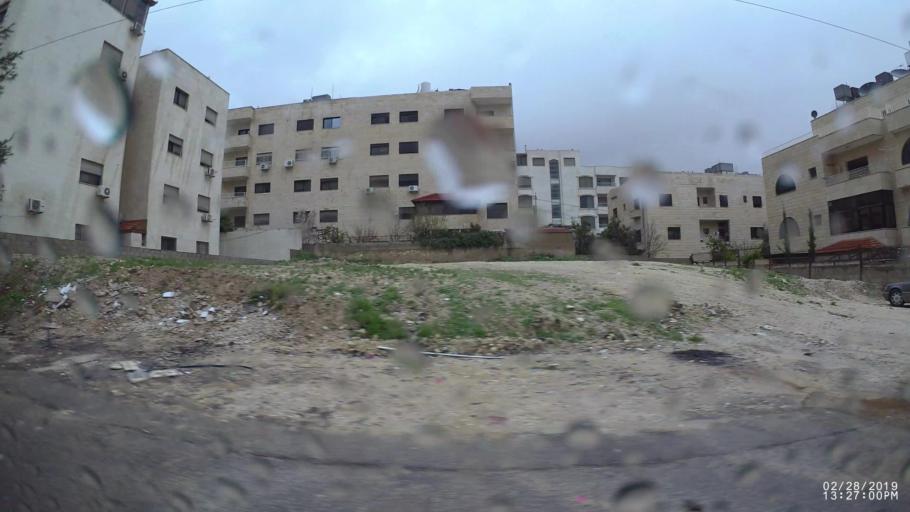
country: JO
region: Amman
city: Al Jubayhah
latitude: 32.0167
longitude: 35.8769
